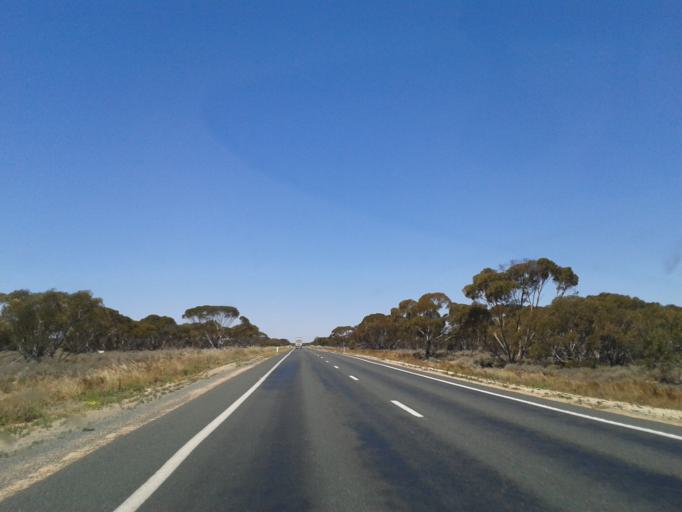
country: AU
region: New South Wales
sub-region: Wentworth
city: Gol Gol
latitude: -34.4861
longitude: 142.5639
